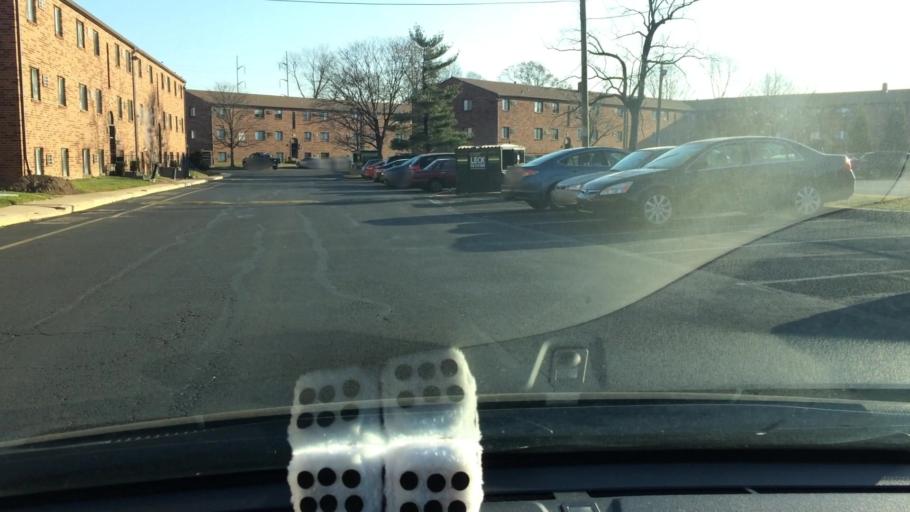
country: US
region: Pennsylvania
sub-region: Montgomery County
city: Rockledge
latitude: 40.0824
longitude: -75.0372
